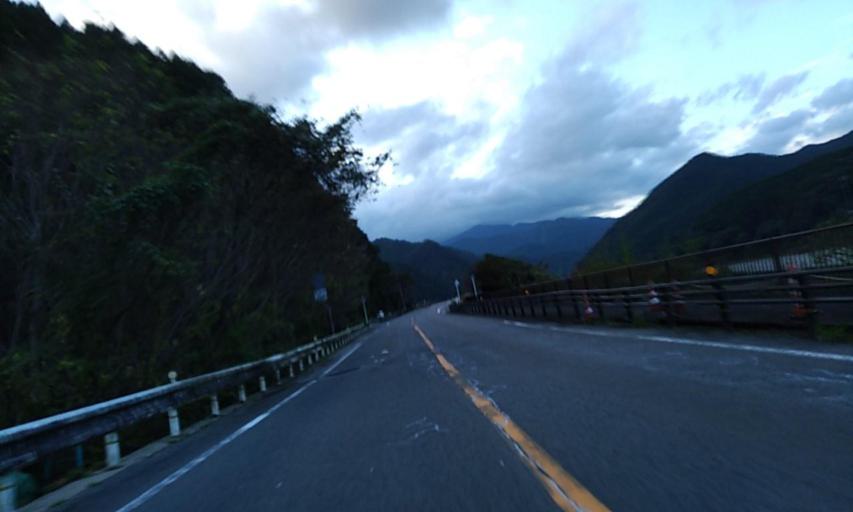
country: JP
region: Wakayama
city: Shingu
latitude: 33.7237
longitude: 135.9632
